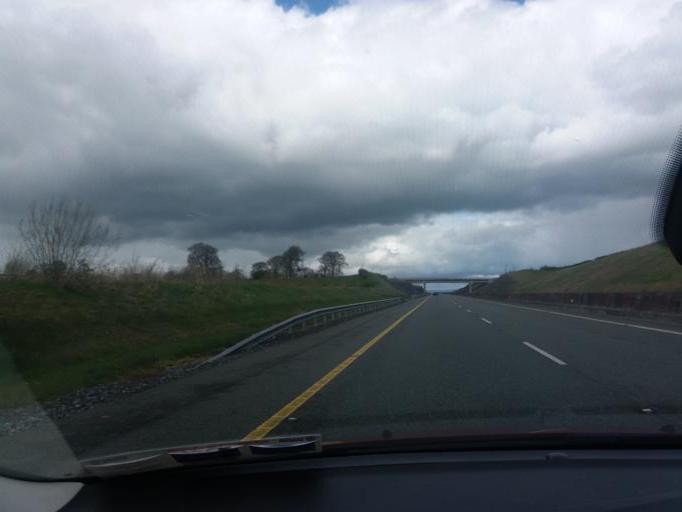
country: IE
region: Leinster
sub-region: Laois
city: Rathdowney
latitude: 52.8211
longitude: -7.4952
